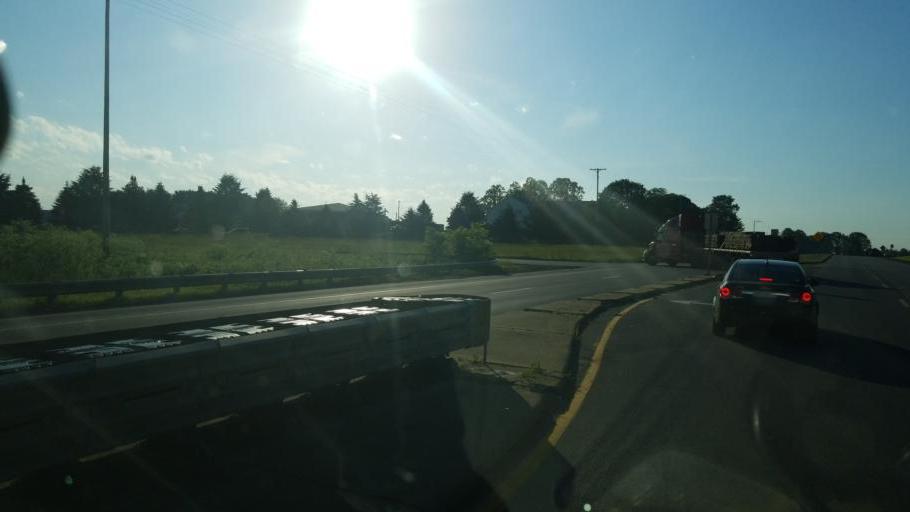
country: US
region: Ohio
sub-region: Wayne County
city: Wooster
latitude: 40.7708
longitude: -81.9140
